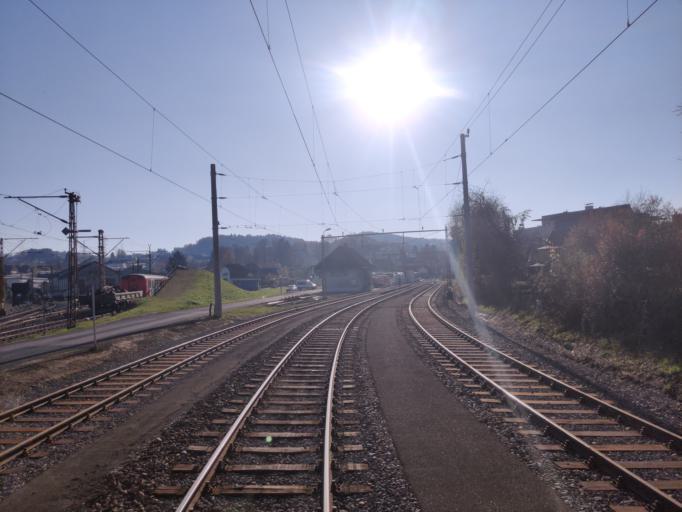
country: AT
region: Styria
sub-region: Politischer Bezirk Suedoststeiermark
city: Feldbach
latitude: 46.9498
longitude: 15.8973
